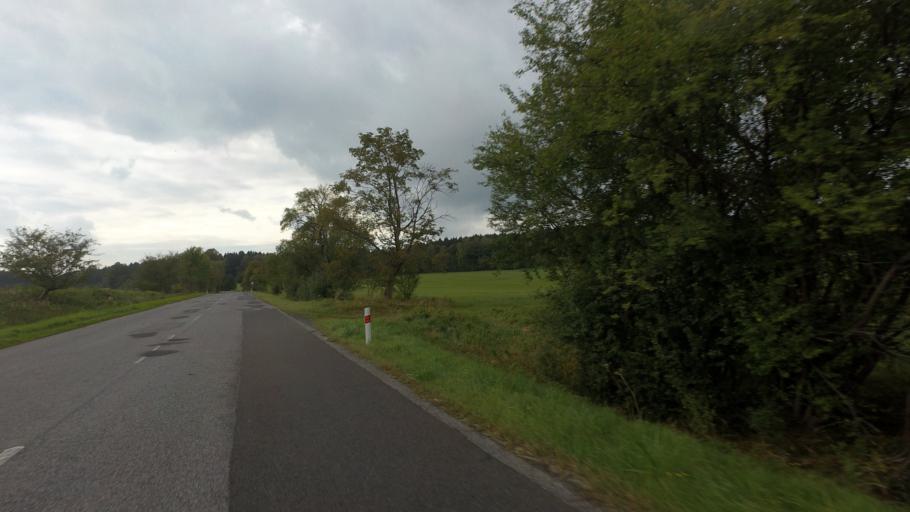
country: CZ
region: Ustecky
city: Vilemov
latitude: 51.0148
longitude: 14.3457
